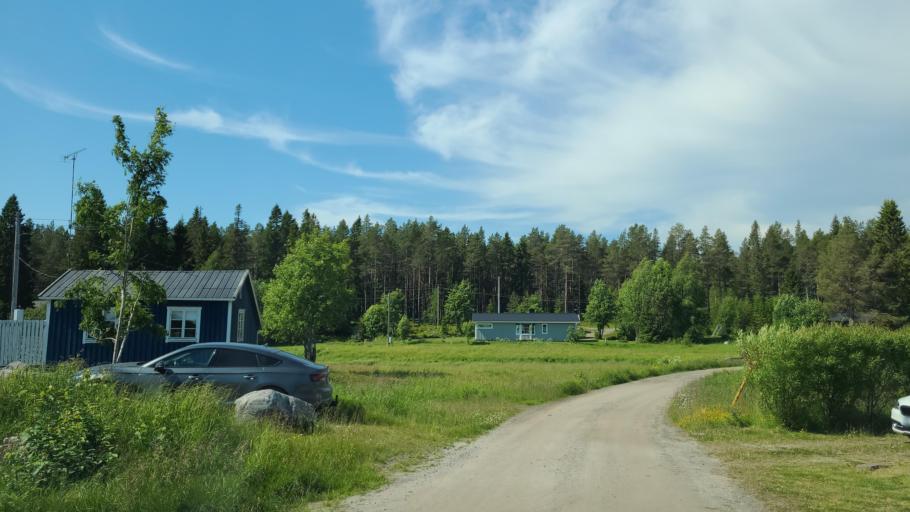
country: SE
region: Vaesterbotten
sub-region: Robertsfors Kommun
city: Robertsfors
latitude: 64.1426
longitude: 20.9648
